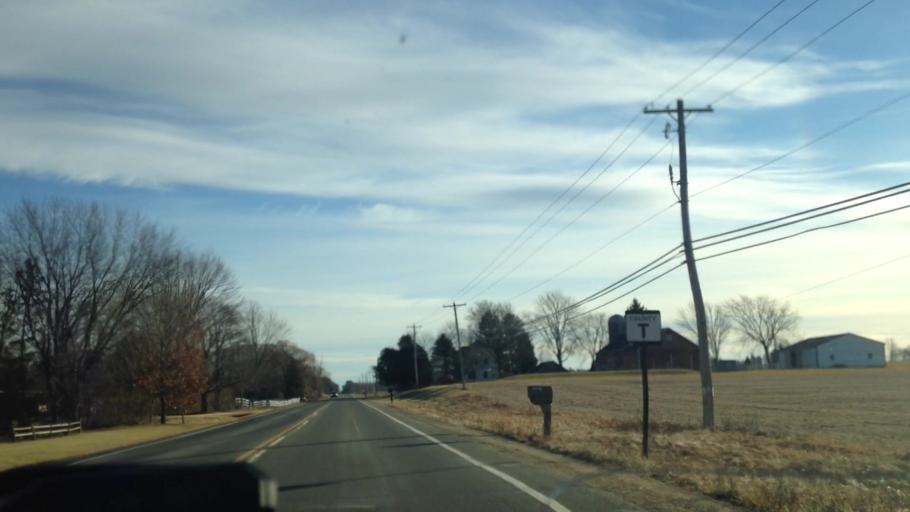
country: US
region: Wisconsin
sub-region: Washington County
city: Germantown
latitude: 43.2937
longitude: -88.0821
